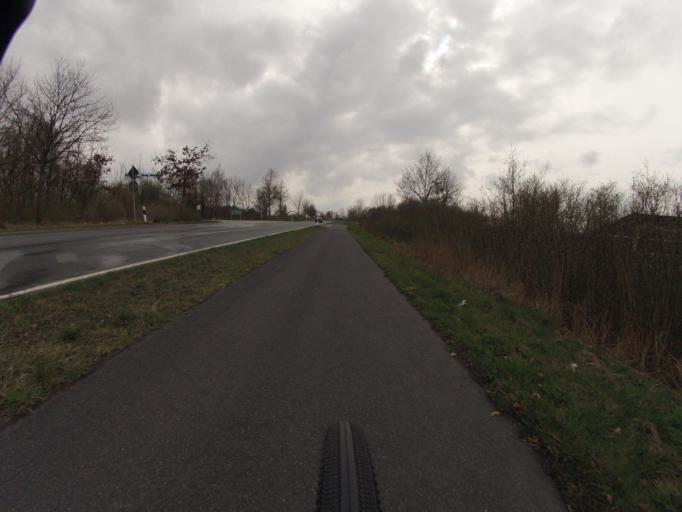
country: DE
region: North Rhine-Westphalia
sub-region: Regierungsbezirk Munster
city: Recke
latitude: 52.3583
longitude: 7.7168
